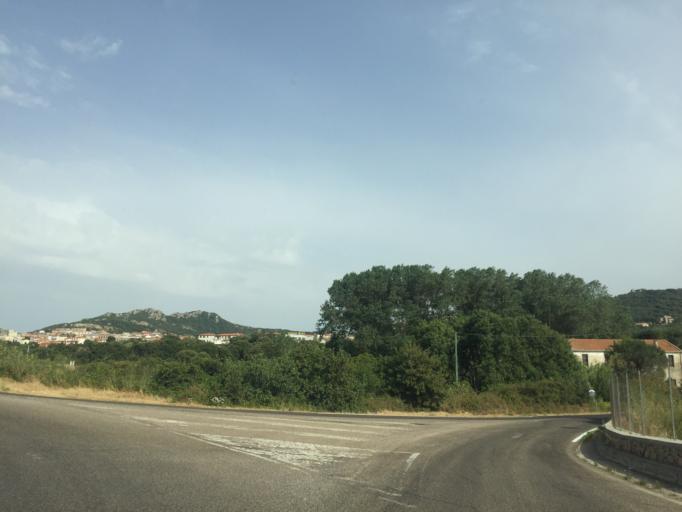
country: IT
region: Sardinia
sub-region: Provincia di Olbia-Tempio
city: Luras
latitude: 40.9248
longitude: 9.1787
